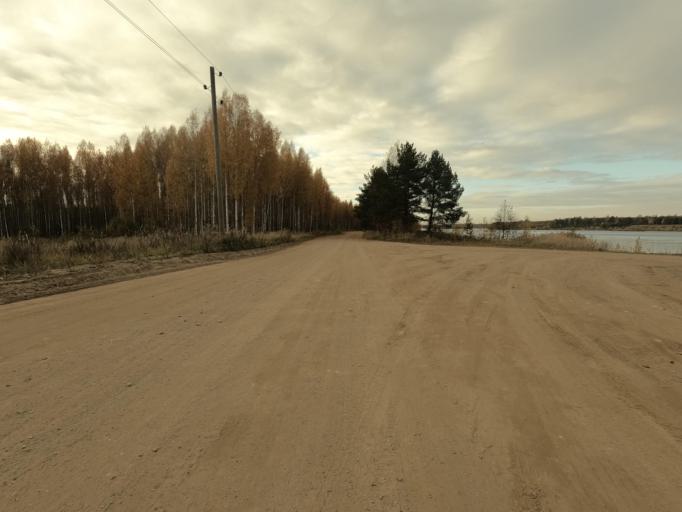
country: RU
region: Leningrad
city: Priladozhskiy
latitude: 59.7114
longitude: 31.3571
